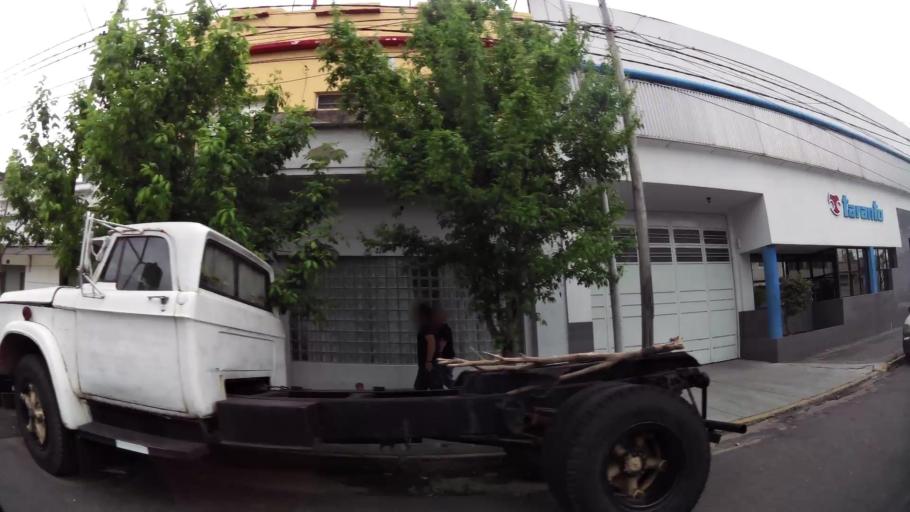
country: AR
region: Buenos Aires
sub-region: Partido de Avellaneda
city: Avellaneda
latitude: -34.6742
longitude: -58.3901
